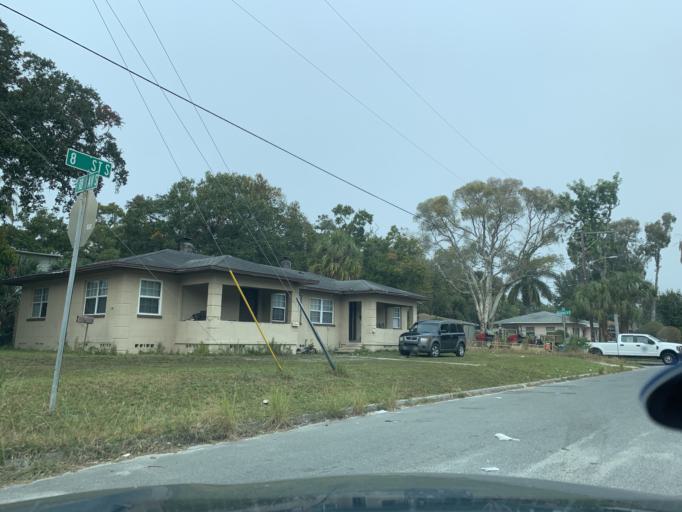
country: US
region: Florida
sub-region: Pinellas County
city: Saint Petersburg
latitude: 27.7522
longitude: -82.6445
